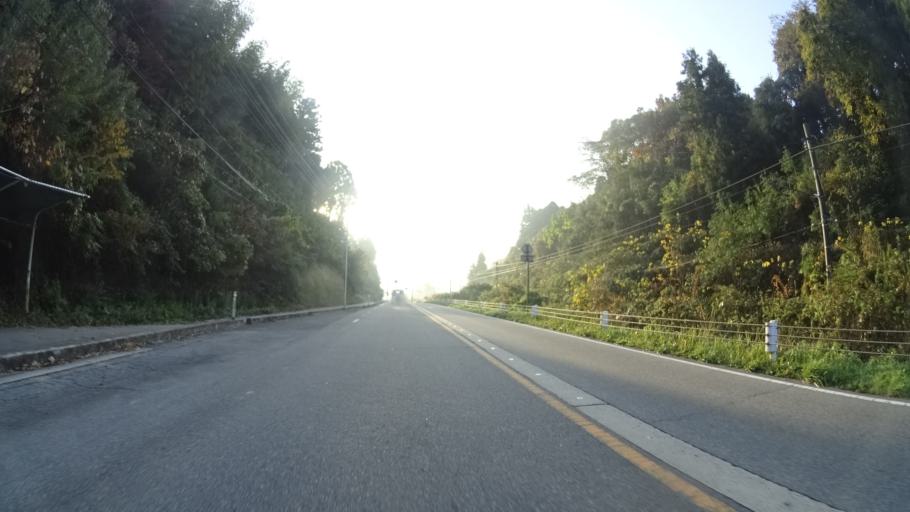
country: JP
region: Ishikawa
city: Nanao
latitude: 37.0595
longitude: 136.9455
